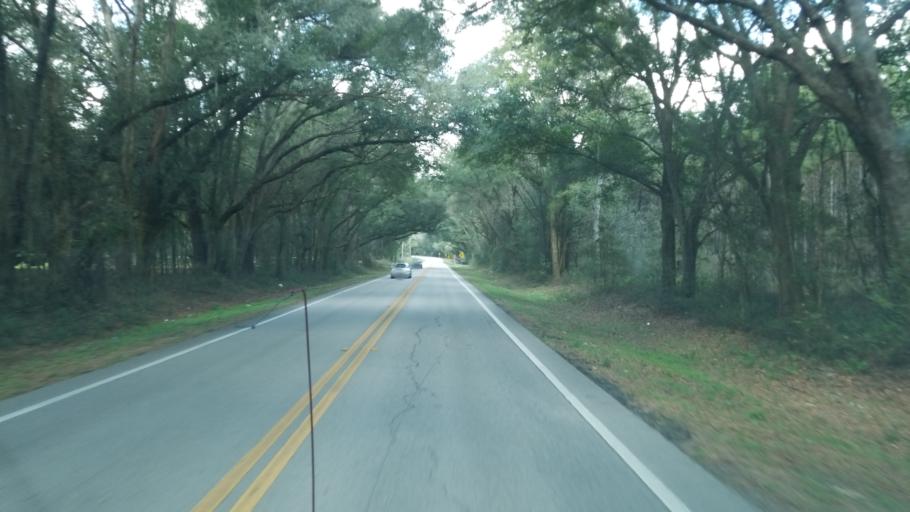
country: US
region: Florida
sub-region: Marion County
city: Belleview
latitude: 29.0610
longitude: -82.1527
